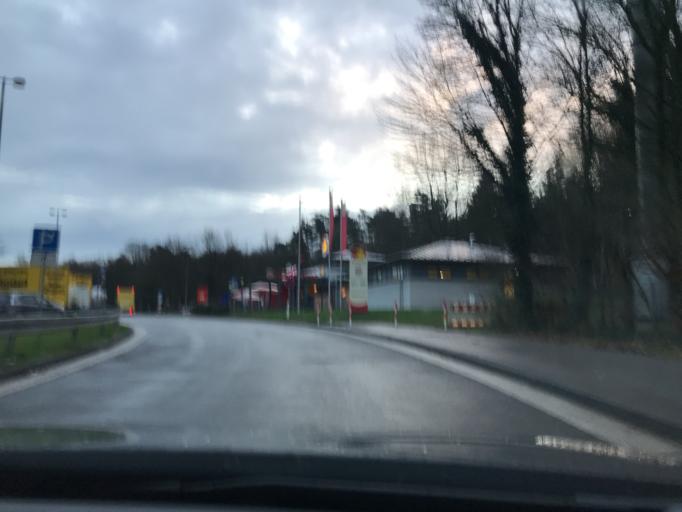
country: DE
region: North Rhine-Westphalia
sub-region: Regierungsbezirk Koln
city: Rosrath
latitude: 50.8984
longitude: 7.1515
